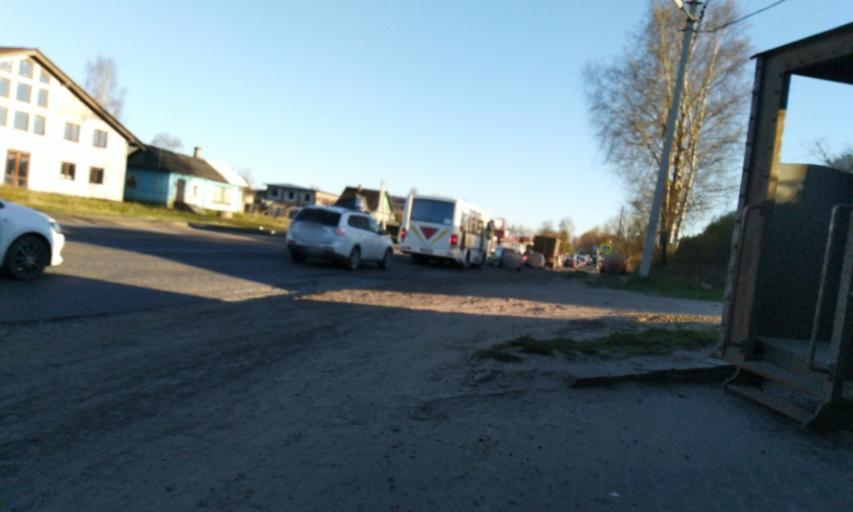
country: RU
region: Leningrad
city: Toksovo
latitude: 60.1148
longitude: 30.5030
